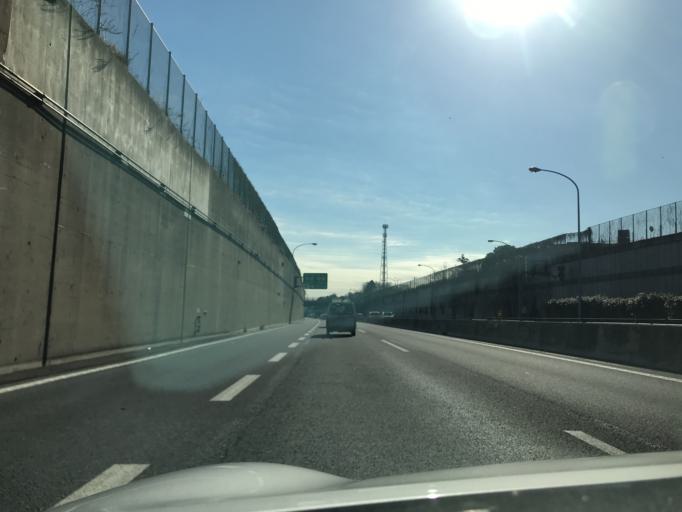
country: JP
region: Chiba
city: Chiba
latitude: 35.6297
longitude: 140.1301
